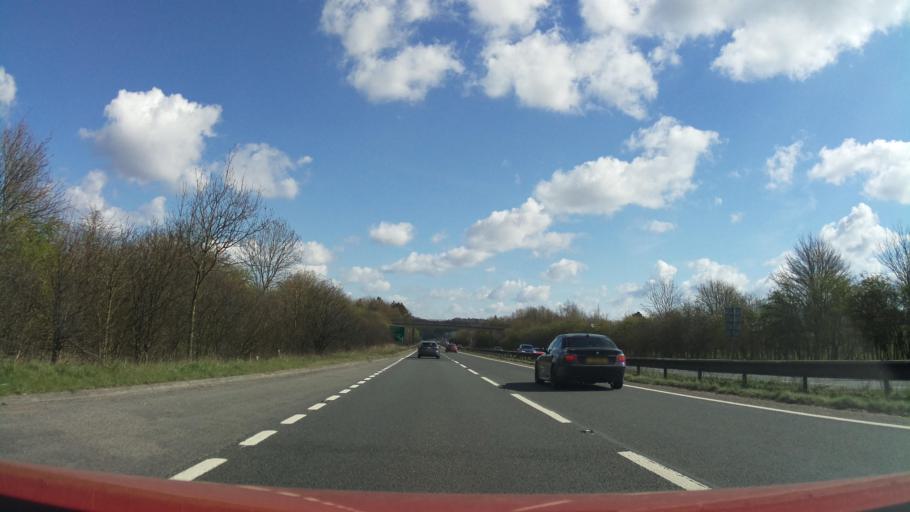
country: GB
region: England
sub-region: Wiltshire
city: Allington
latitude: 51.1879
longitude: -1.6898
